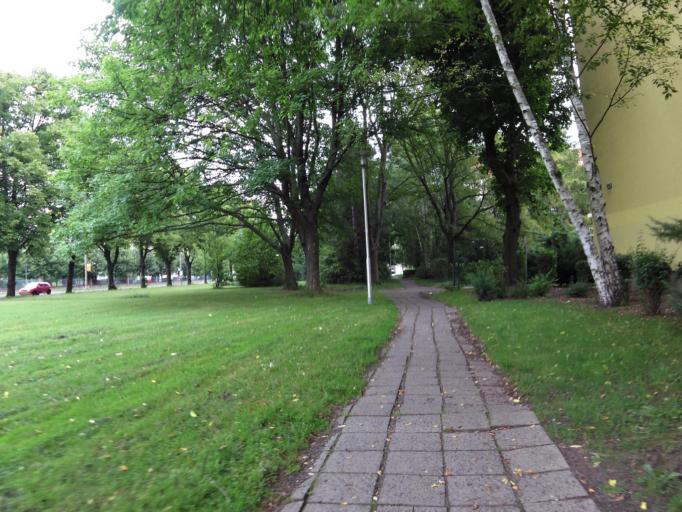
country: DE
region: Saxony
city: Leipzig
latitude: 51.3512
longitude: 12.4284
